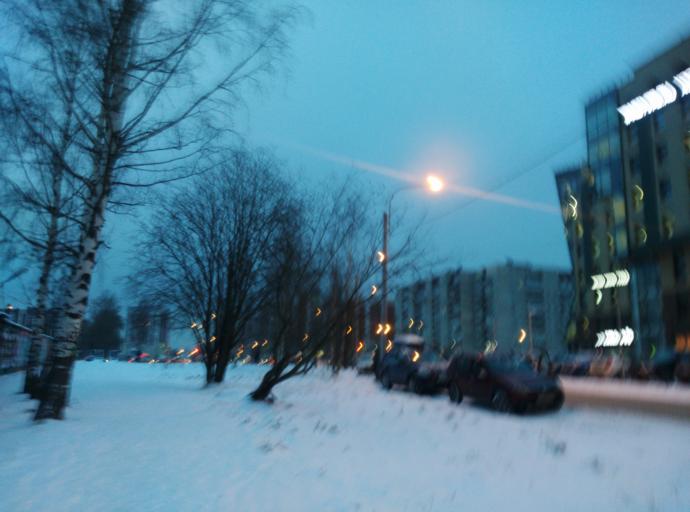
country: RU
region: St.-Petersburg
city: Kolomyagi
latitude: 60.0230
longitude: 30.2977
